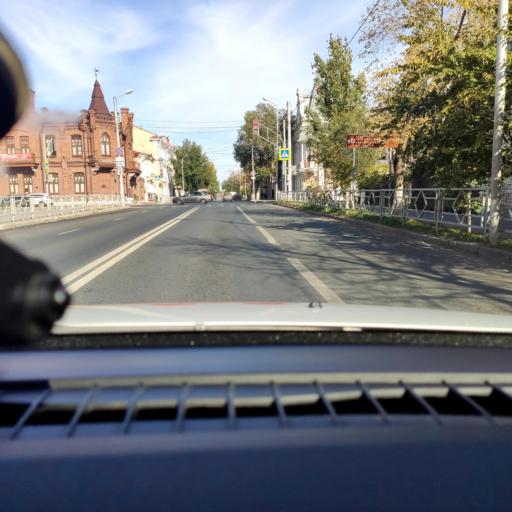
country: RU
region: Samara
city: Rozhdestveno
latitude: 53.1827
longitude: 50.0858
